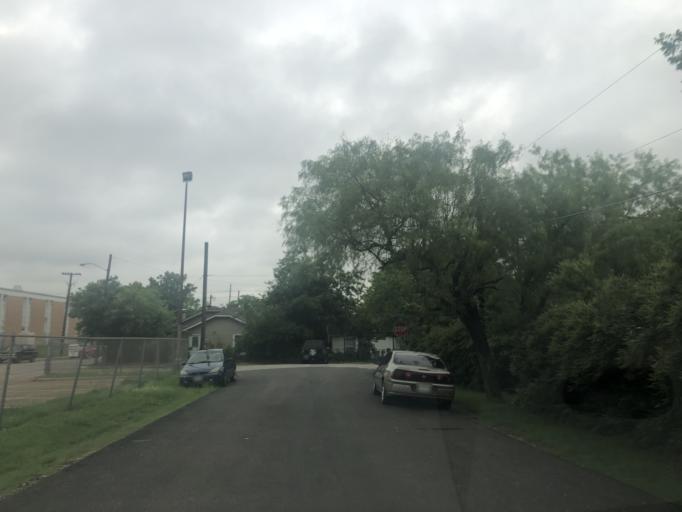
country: US
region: Texas
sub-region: Dallas County
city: Cockrell Hill
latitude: 32.7773
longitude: -96.8673
